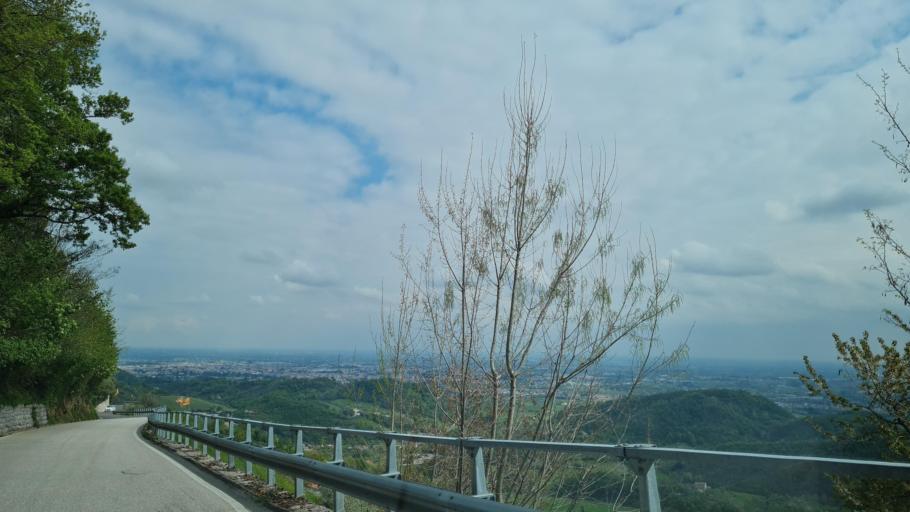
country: IT
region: Veneto
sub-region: Provincia di Vicenza
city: Marostica
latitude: 45.7815
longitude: 11.6726
